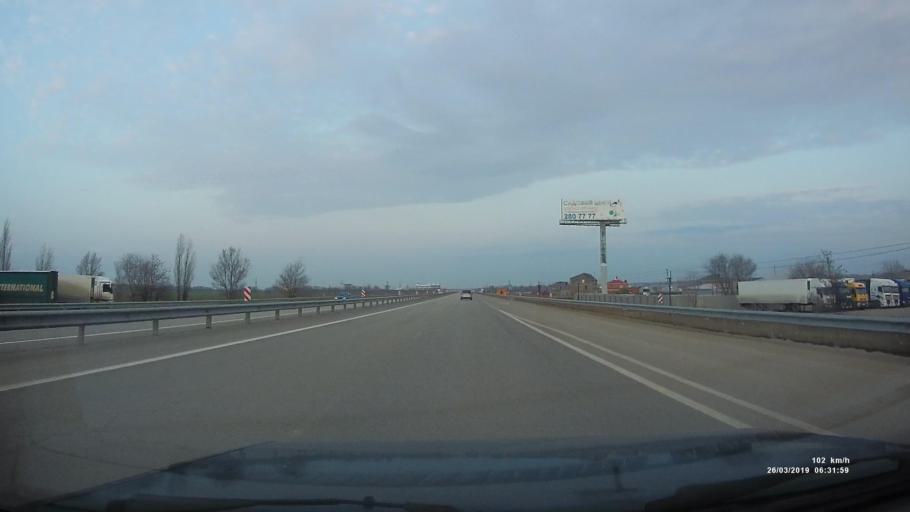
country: RU
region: Rostov
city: Kalinin
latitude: 47.2719
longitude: 39.5199
